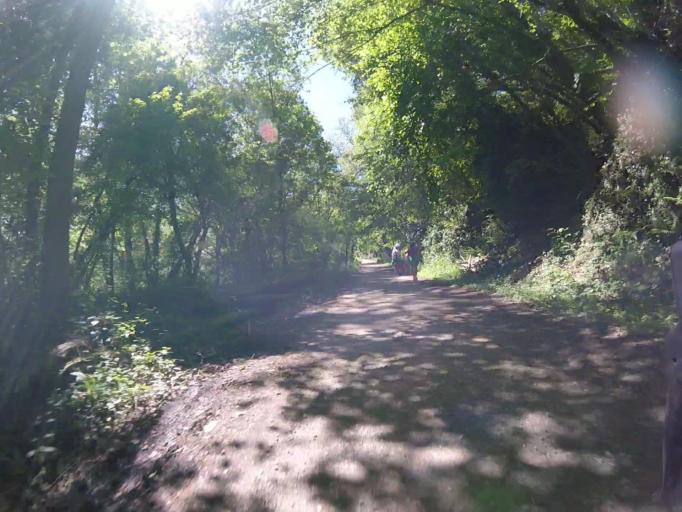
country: ES
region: Navarre
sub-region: Provincia de Navarra
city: Bera
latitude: 43.2781
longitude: -1.7135
